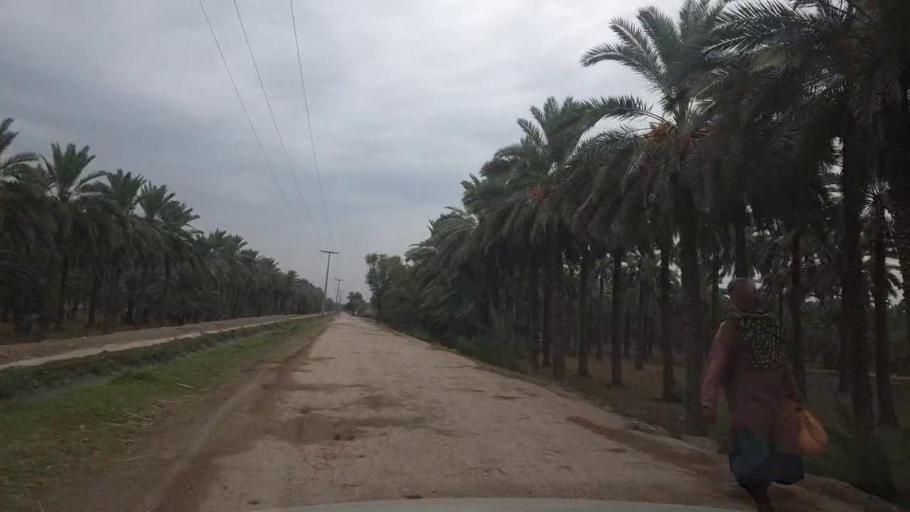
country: PK
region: Sindh
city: Khairpur
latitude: 27.6087
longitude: 68.8169
